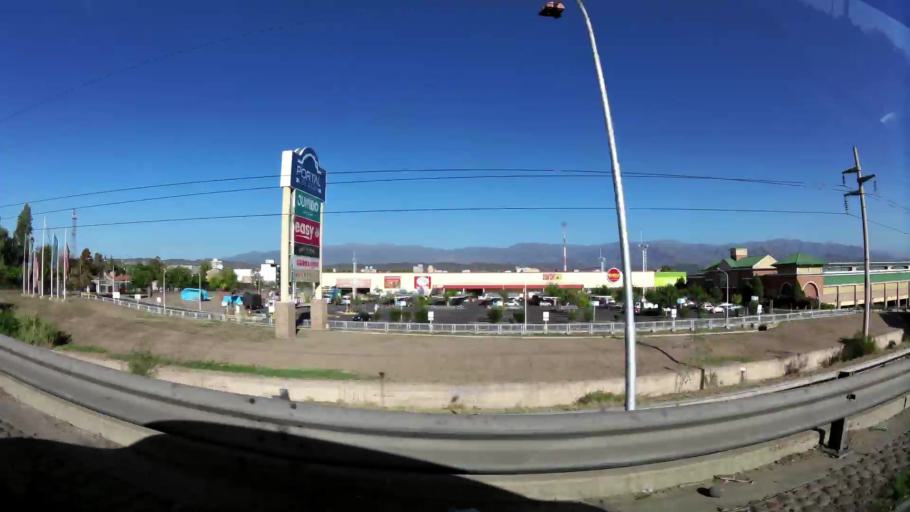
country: AR
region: Mendoza
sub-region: Departamento de Godoy Cruz
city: Godoy Cruz
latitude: -32.9179
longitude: -68.8375
